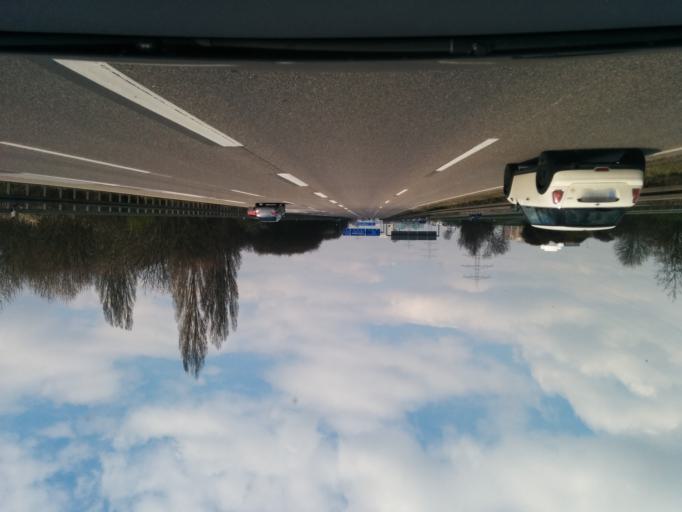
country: DE
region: Hesse
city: Sulzbach
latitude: 50.1227
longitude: 8.5528
